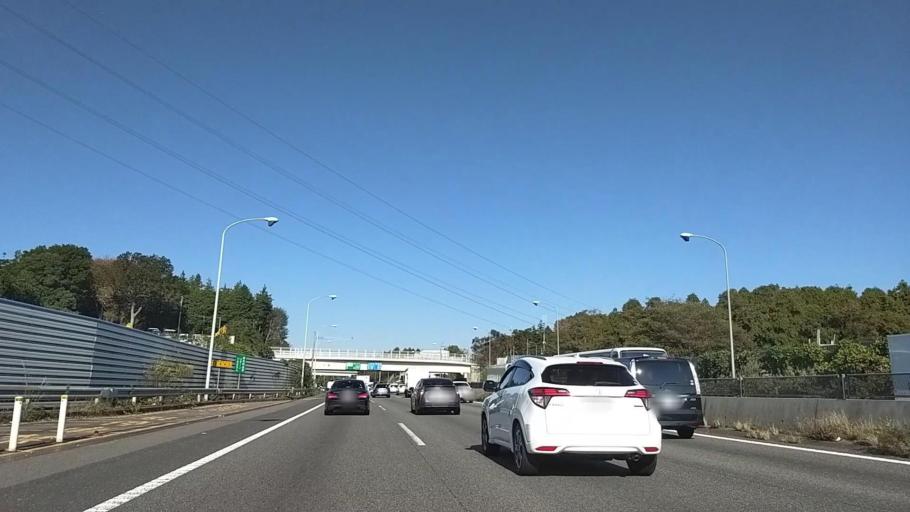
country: JP
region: Kanagawa
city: Minami-rinkan
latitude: 35.4888
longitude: 139.5065
